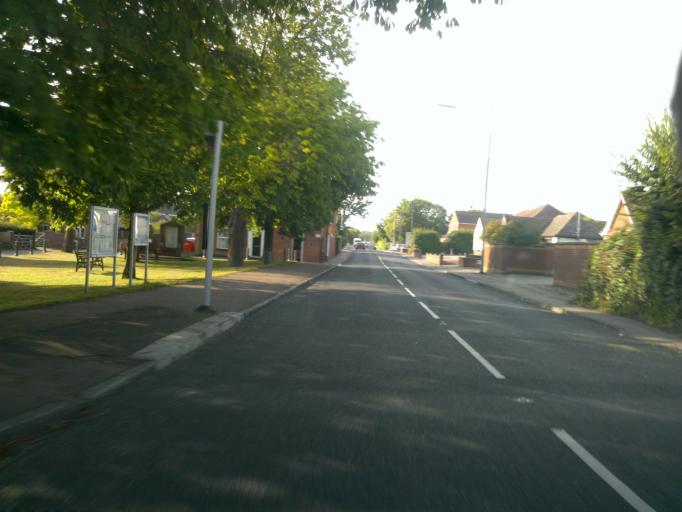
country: GB
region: England
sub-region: Essex
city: Little Clacton
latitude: 51.8275
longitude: 1.1418
